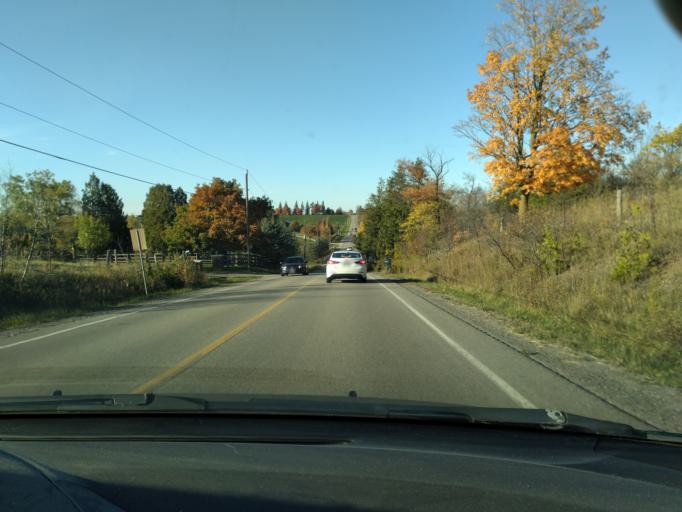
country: CA
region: Ontario
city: Bradford West Gwillimbury
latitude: 43.9835
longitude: -79.7235
